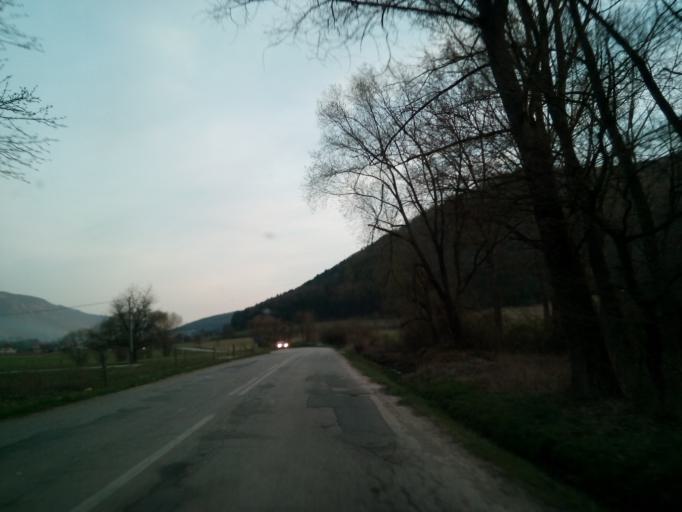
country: SK
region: Kosicky
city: Dobsina
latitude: 48.6699
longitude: 20.3577
